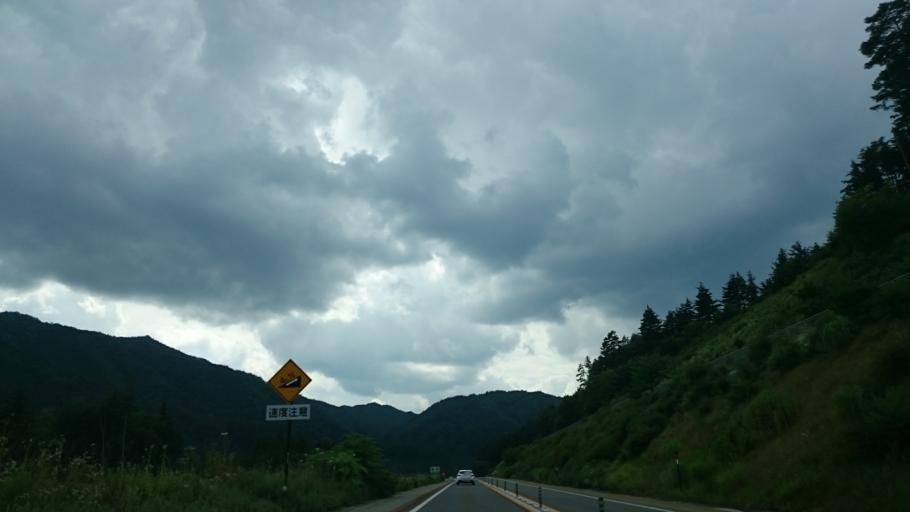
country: JP
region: Gifu
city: Takayama
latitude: 36.1402
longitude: 137.1500
